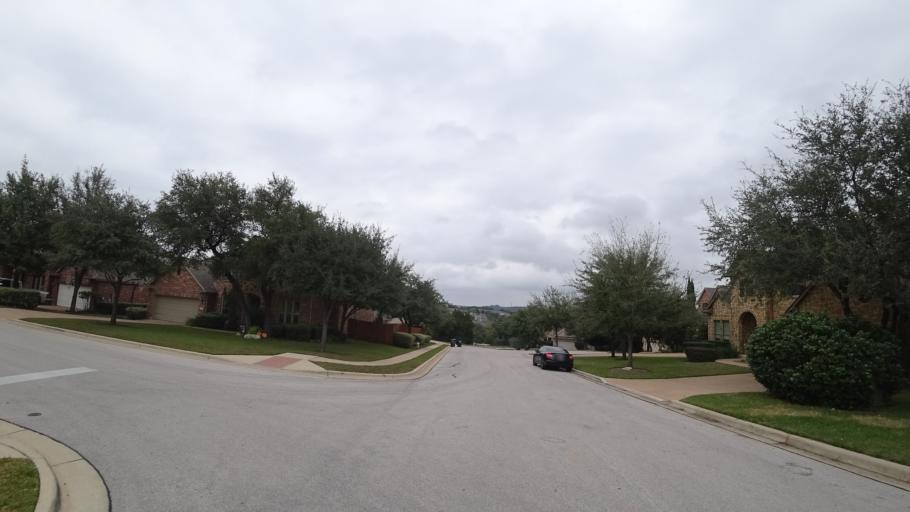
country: US
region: Texas
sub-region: Travis County
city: Hudson Bend
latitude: 30.3590
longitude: -97.9062
